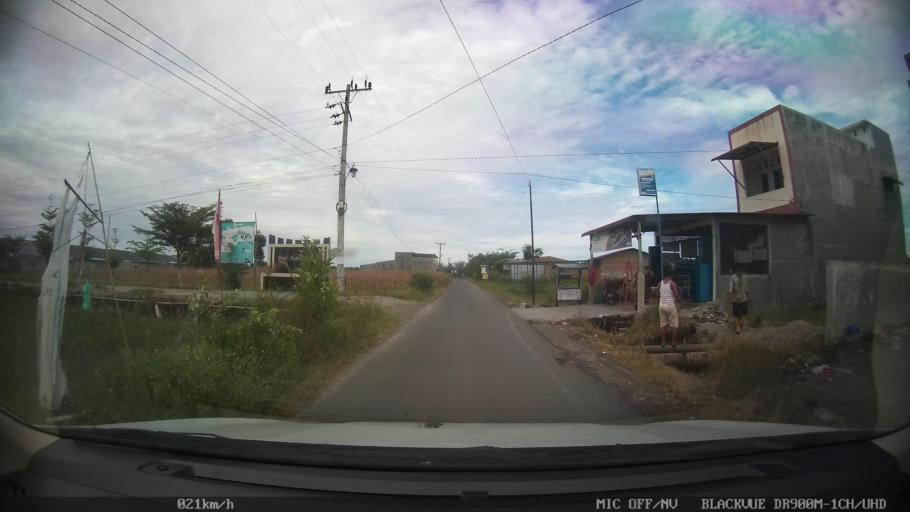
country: ID
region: North Sumatra
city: Sunggal
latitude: 3.5726
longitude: 98.5734
